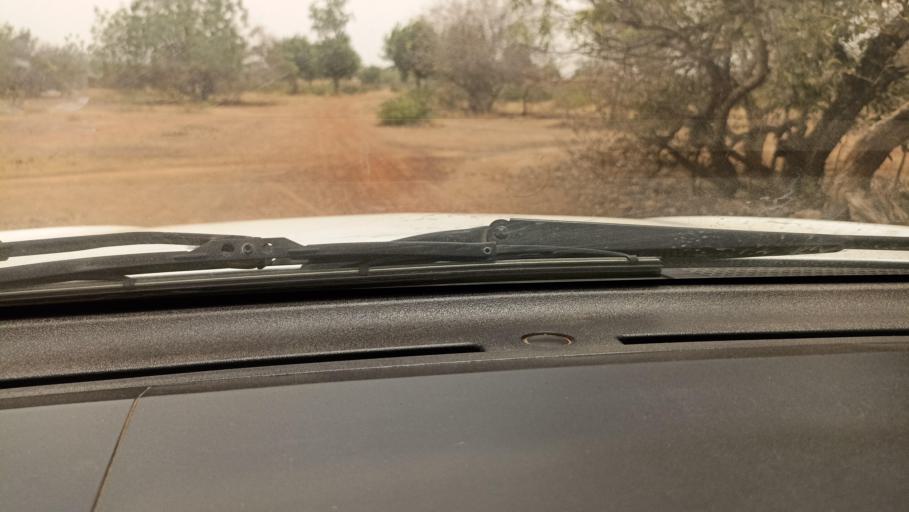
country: BF
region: Boucle du Mouhoun
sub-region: Province du Nayala
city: Toma
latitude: 12.8671
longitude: -2.7494
